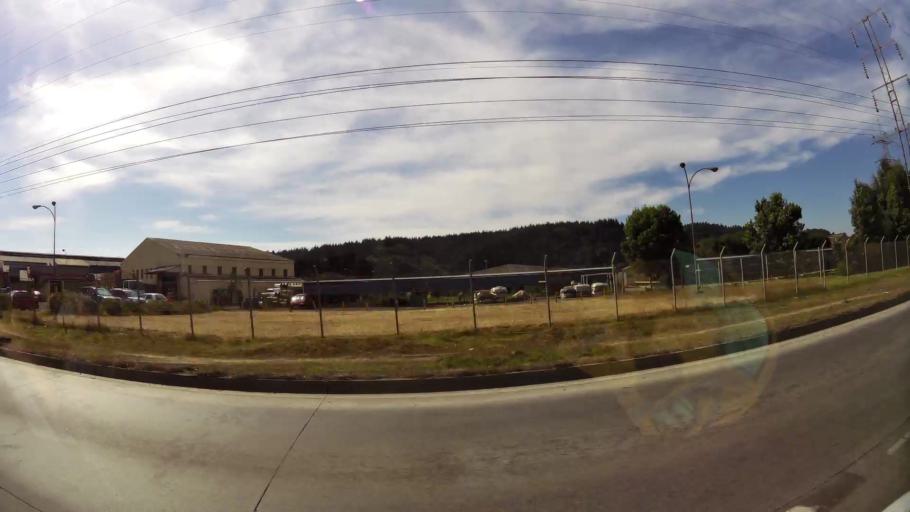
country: CL
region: Biobio
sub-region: Provincia de Concepcion
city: Talcahuano
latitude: -36.7468
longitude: -73.1229
